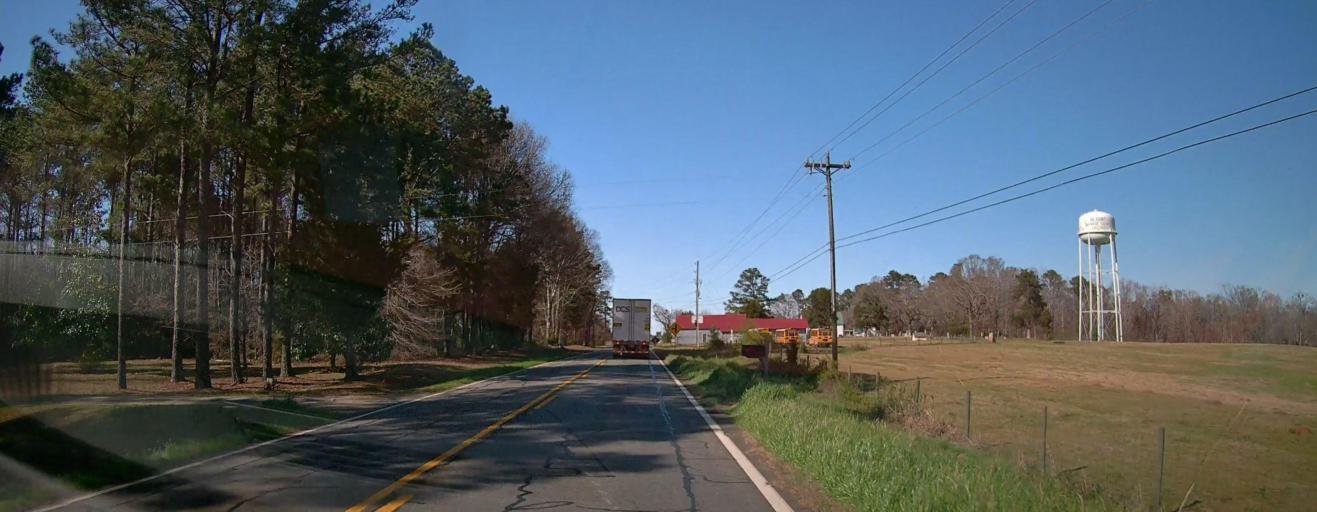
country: US
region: Georgia
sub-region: Butts County
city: Indian Springs
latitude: 33.1751
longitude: -83.9588
